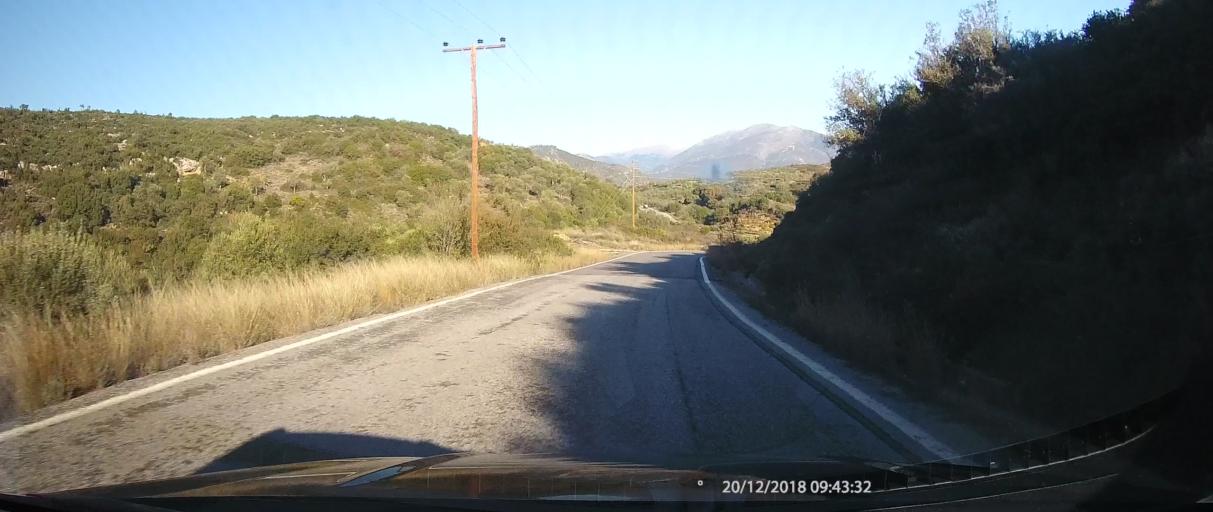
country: GR
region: Peloponnese
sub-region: Nomos Lakonias
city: Yerakion
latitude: 36.9659
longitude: 22.7437
